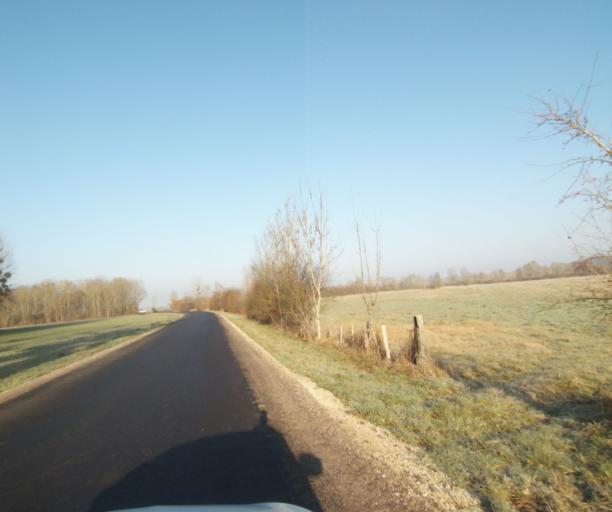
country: FR
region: Champagne-Ardenne
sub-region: Departement de la Haute-Marne
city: Montier-en-Der
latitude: 48.4902
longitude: 4.7356
